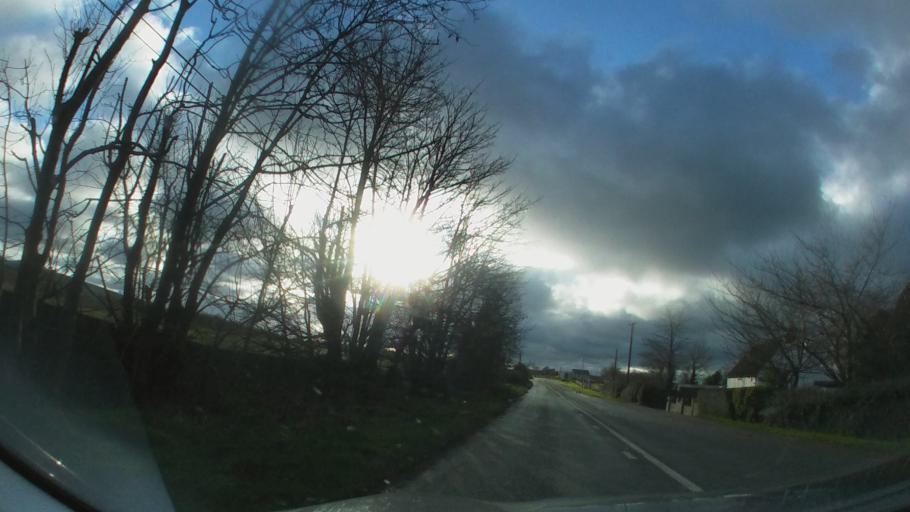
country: IE
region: Leinster
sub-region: Kilkenny
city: Thomastown
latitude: 52.6047
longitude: -7.0890
